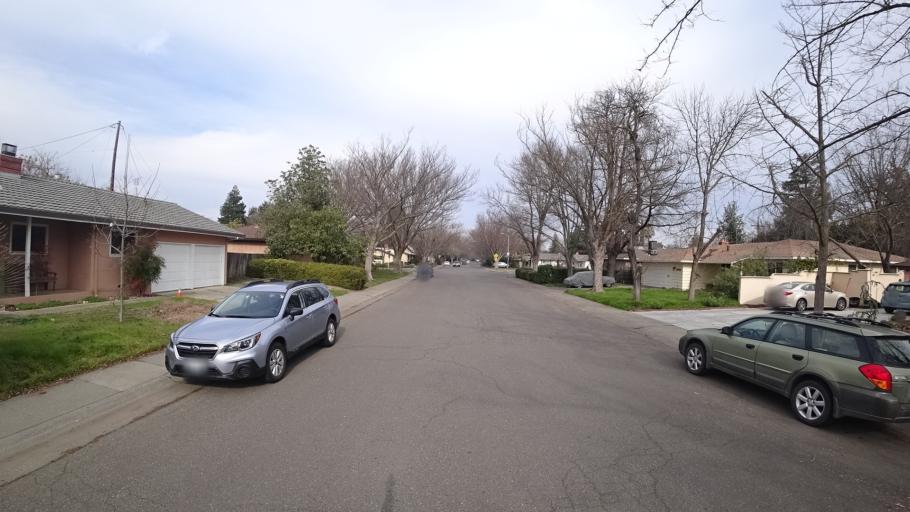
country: US
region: California
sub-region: Yolo County
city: Davis
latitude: 38.5552
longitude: -121.7319
